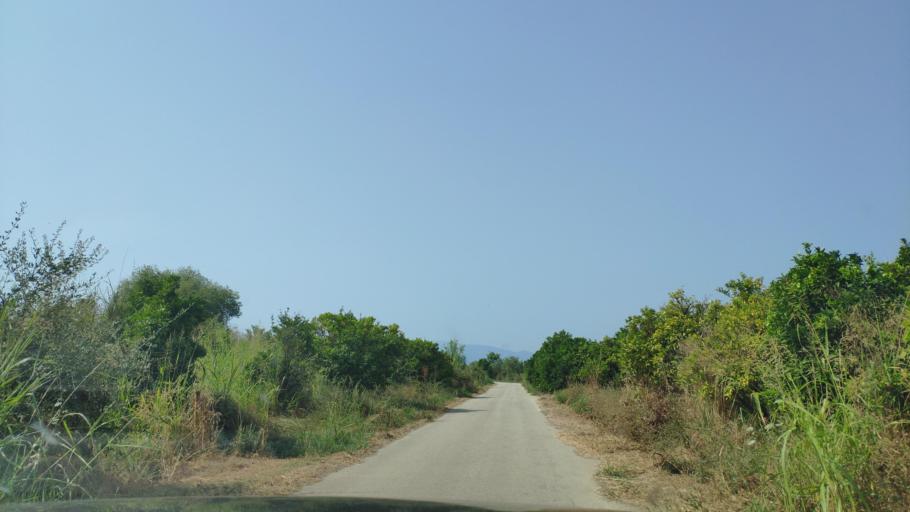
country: GR
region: Epirus
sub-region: Nomos Artas
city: Kompoti
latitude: 39.0598
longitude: 21.0731
